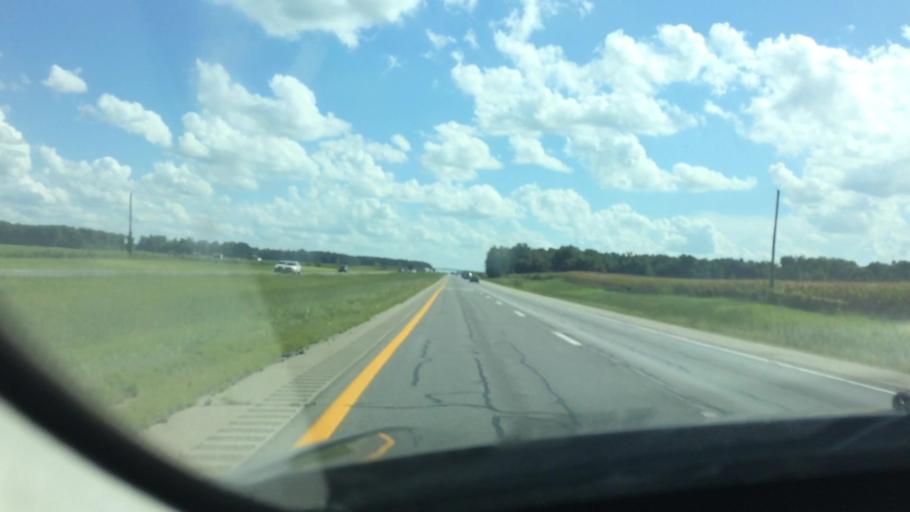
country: US
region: Ohio
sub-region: Shelby County
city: Botkins
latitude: 40.5098
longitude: -84.1694
